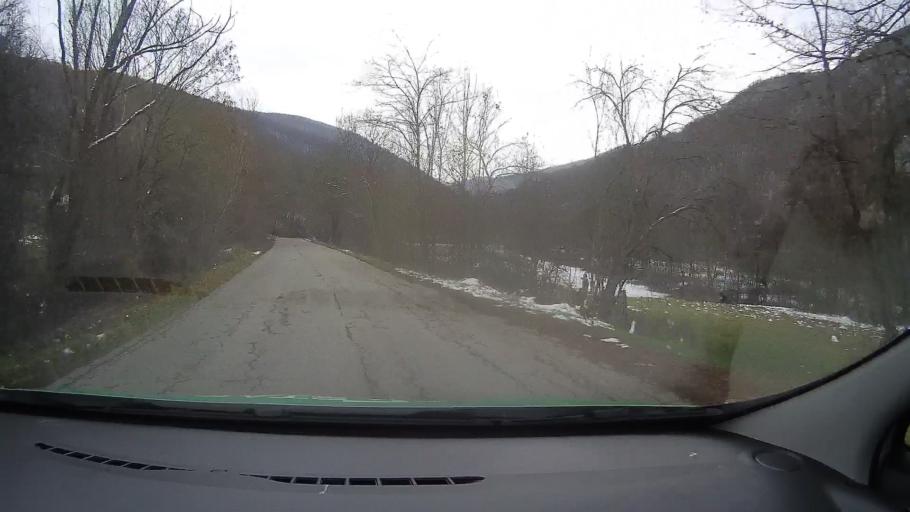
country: RO
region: Hunedoara
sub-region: Comuna Balsa
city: Balsa
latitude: 46.0154
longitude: 23.1492
